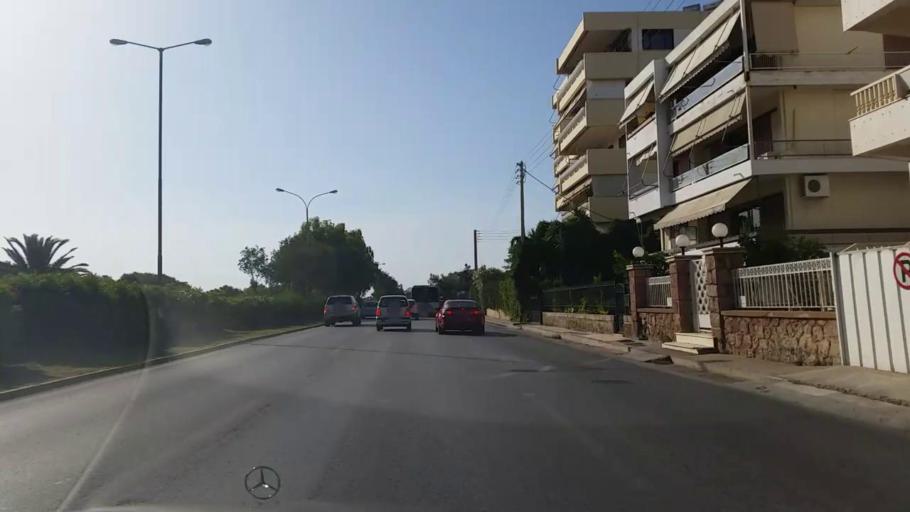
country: GR
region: Attica
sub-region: Nomarchia Anatolikis Attikis
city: Voula
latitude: 37.8413
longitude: 23.7600
